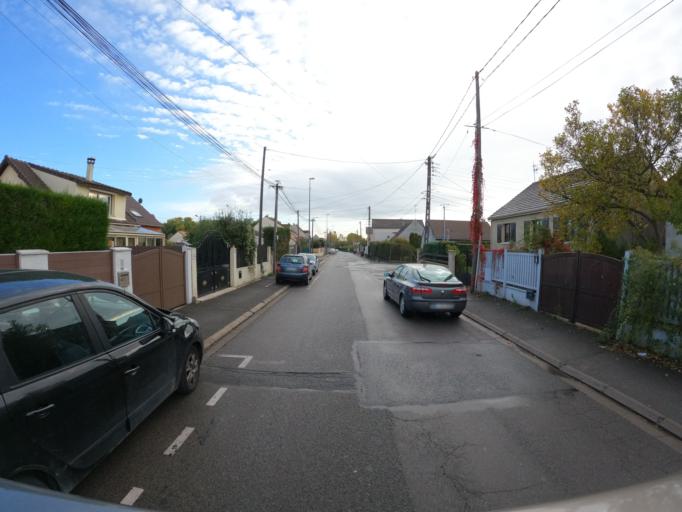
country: FR
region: Ile-de-France
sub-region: Departement de Seine-et-Marne
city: Courtry
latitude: 48.9035
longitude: 2.6065
